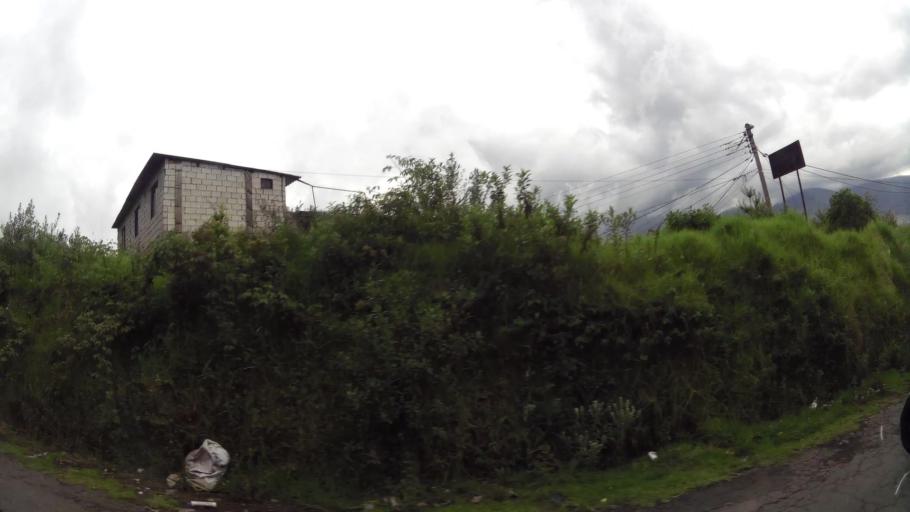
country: EC
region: Pichincha
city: Sangolqui
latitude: -0.3177
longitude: -78.5325
